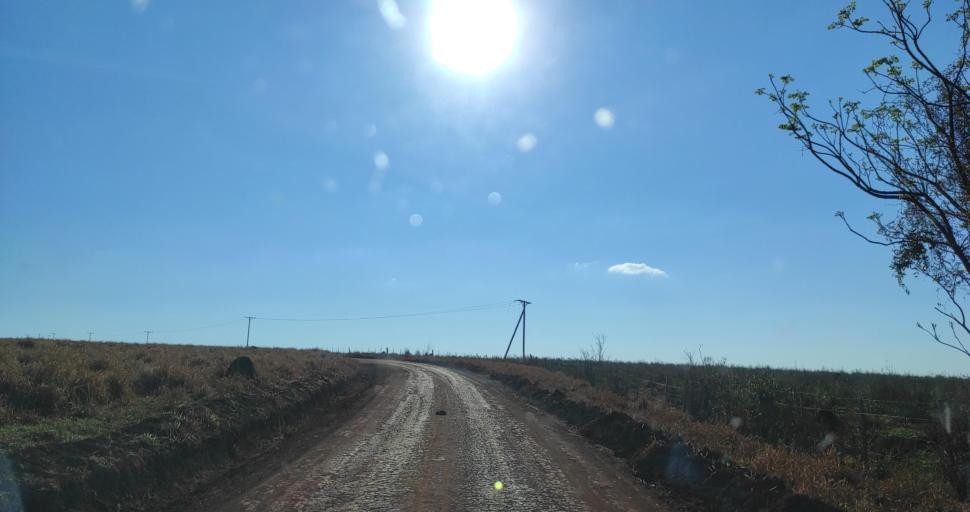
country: PY
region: Itapua
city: San Juan del Parana
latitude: -27.4367
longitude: -56.0630
